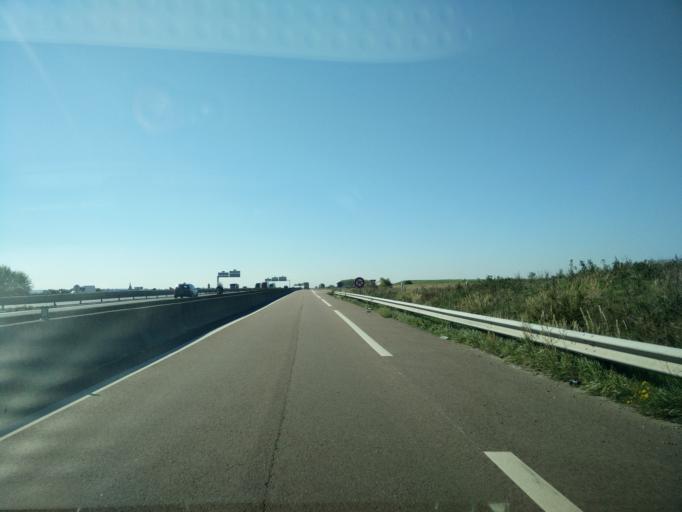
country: FR
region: Ile-de-France
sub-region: Departement de Seine-et-Marne
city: Mitry-Mory
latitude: 48.9985
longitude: 2.6333
